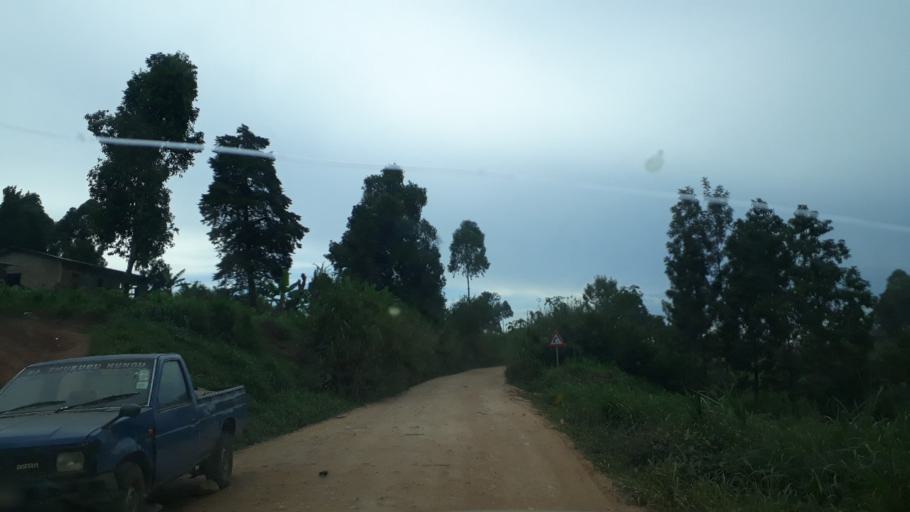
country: CD
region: Eastern Province
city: Bunia
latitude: 1.9130
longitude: 30.5045
